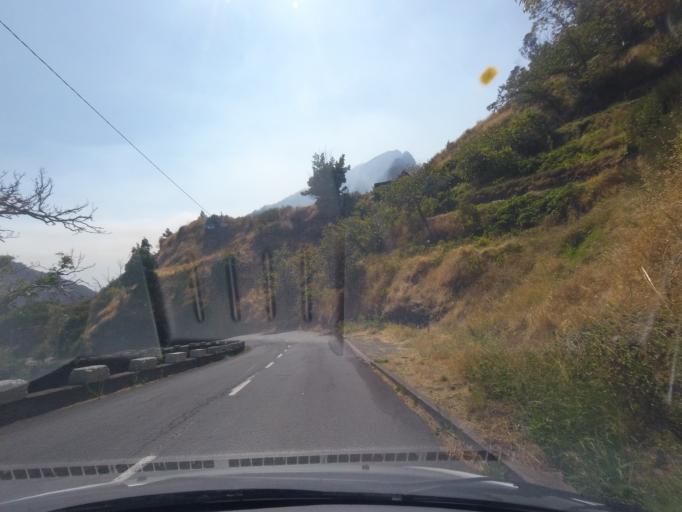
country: PT
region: Madeira
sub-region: Camara de Lobos
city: Curral das Freiras
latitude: 32.7325
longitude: -17.0242
